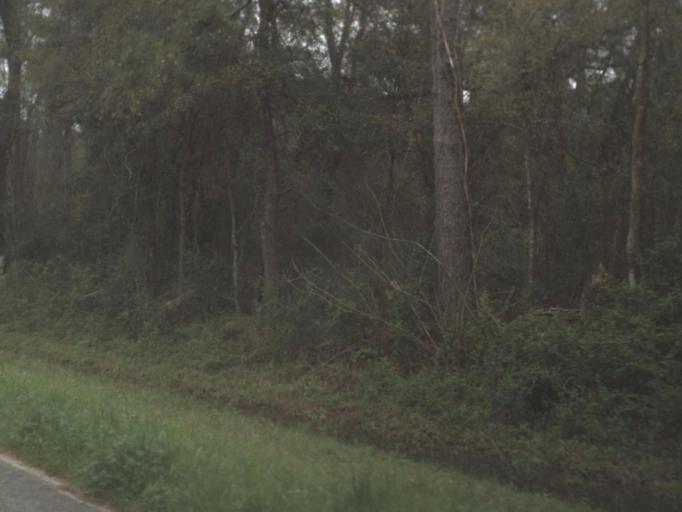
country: US
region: Florida
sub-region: Gadsden County
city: Gretna
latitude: 30.5253
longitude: -84.6890
